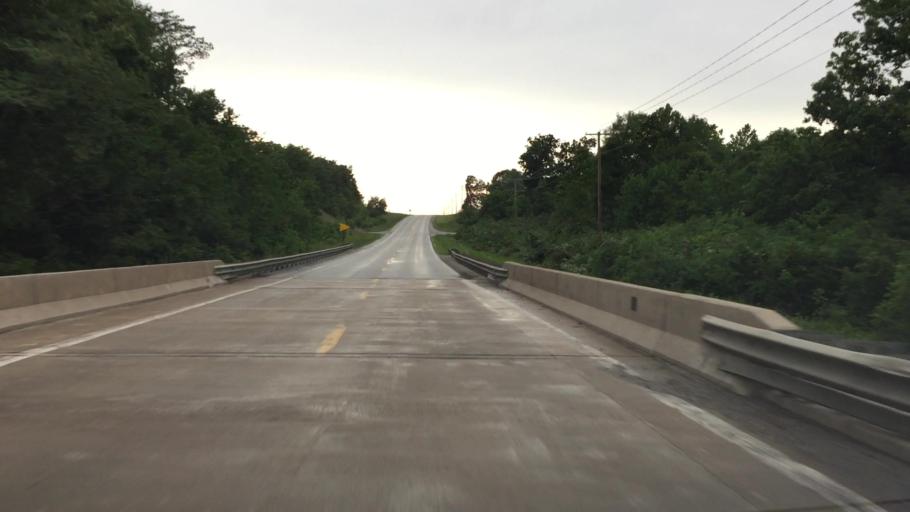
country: US
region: Illinois
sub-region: Hancock County
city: Hamilton
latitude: 40.3614
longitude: -91.3589
